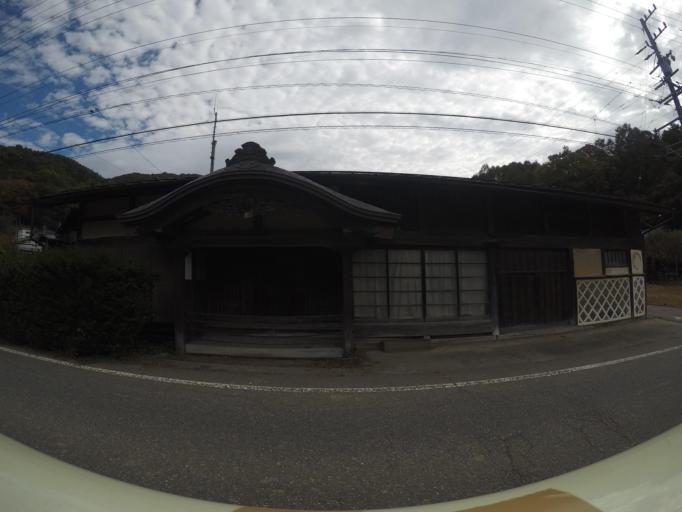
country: JP
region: Nagano
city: Chino
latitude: 35.9261
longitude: 138.0985
